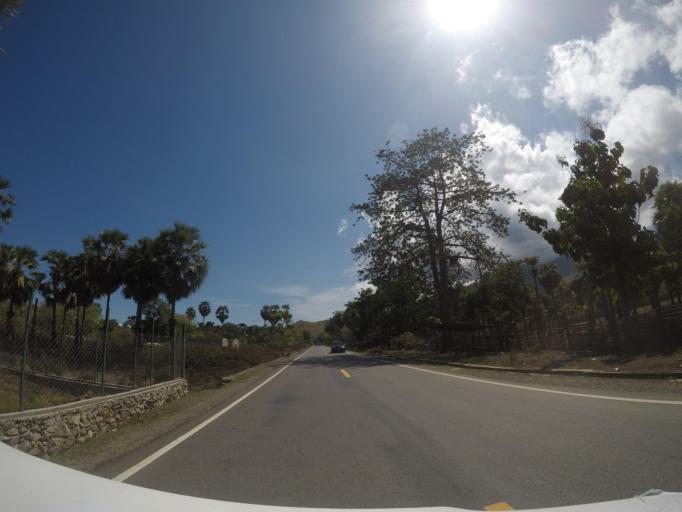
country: ID
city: Metinaro
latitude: -8.4946
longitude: 125.8262
